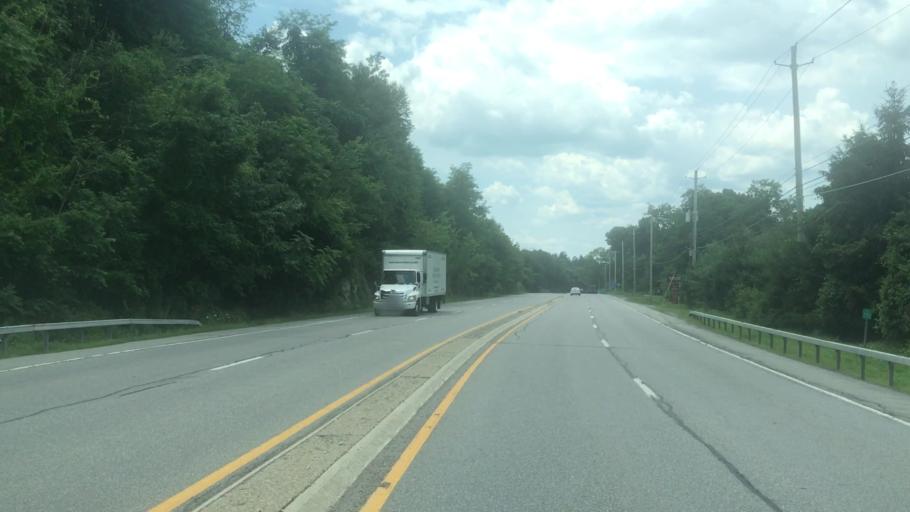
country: US
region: New York
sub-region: Putnam County
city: Peach Lake
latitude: 41.3851
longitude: -73.5783
